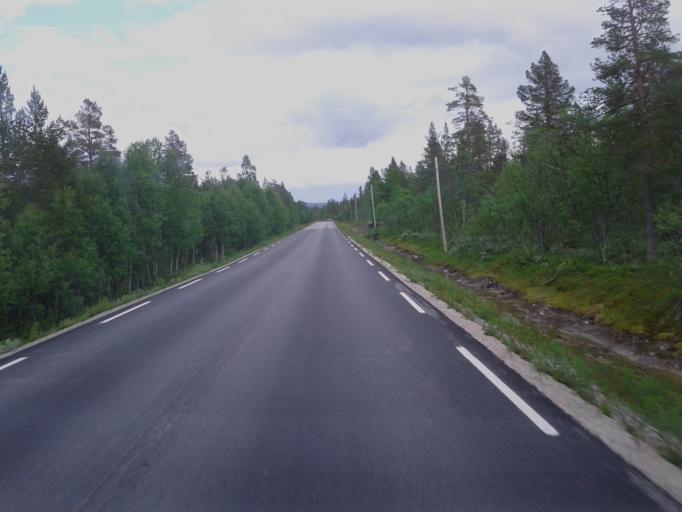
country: NO
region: Sor-Trondelag
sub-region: Roros
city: Roros
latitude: 62.3109
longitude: 11.6736
